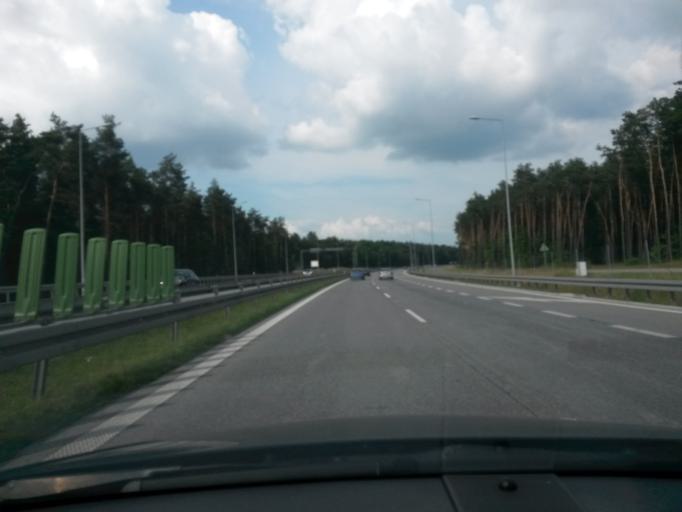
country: PL
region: Lodz Voivodeship
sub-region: Powiat tomaszowski
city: Lubochnia
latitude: 51.6255
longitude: 20.0971
